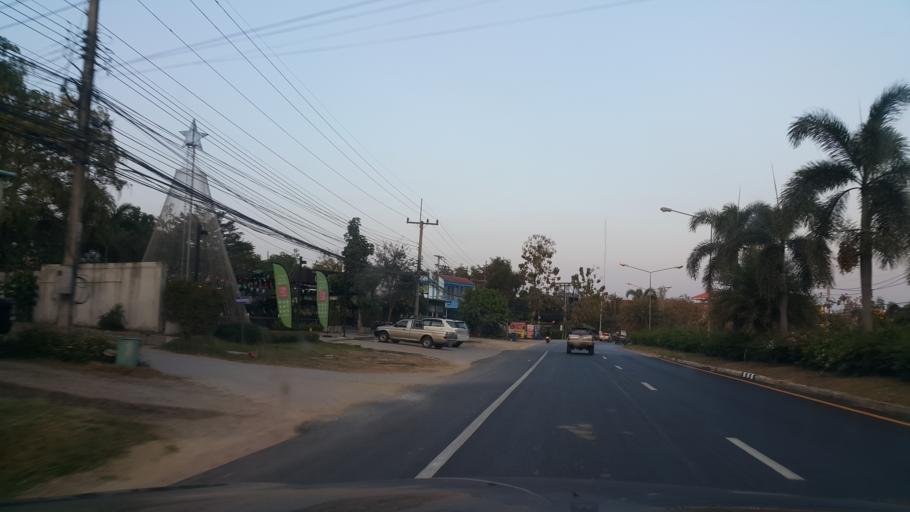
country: TH
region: Loei
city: Loei
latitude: 17.4927
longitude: 101.7061
